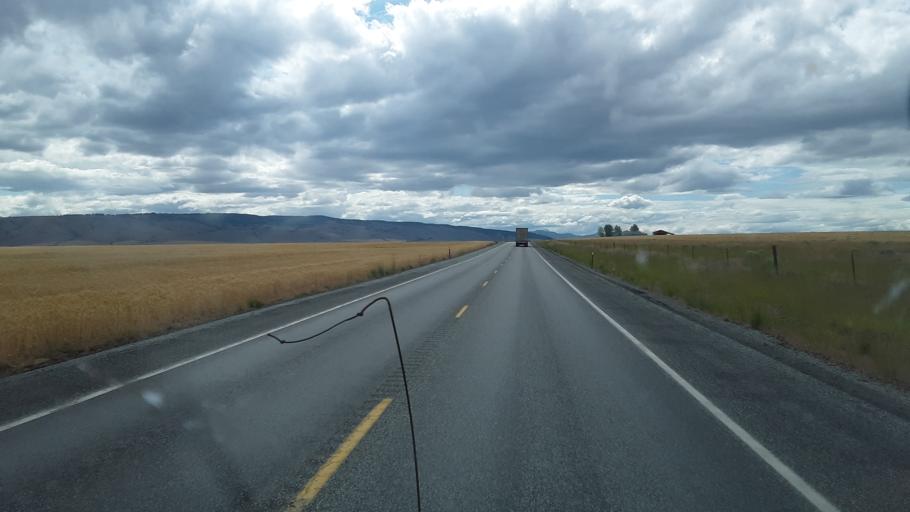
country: US
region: Washington
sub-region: Douglas County
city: Waterville
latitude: 47.6127
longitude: -119.9852
